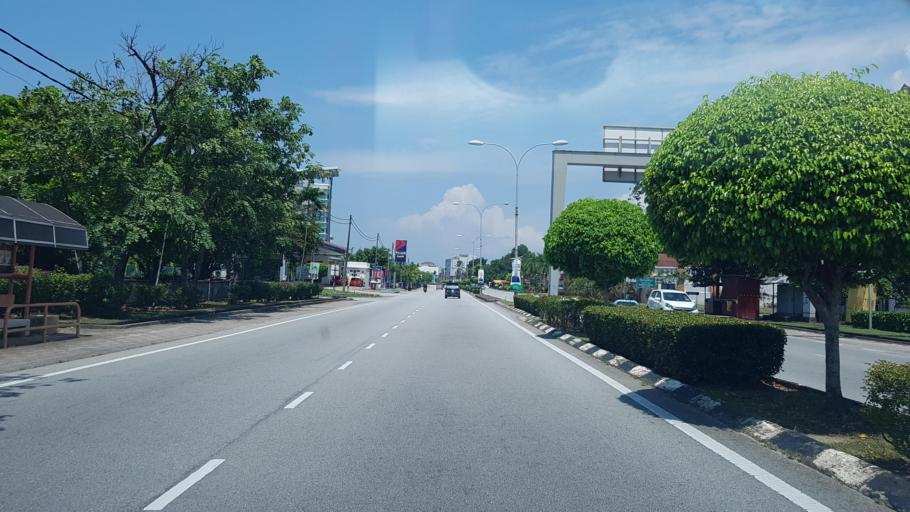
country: MY
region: Terengganu
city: Kuala Terengganu
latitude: 5.3165
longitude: 103.1543
